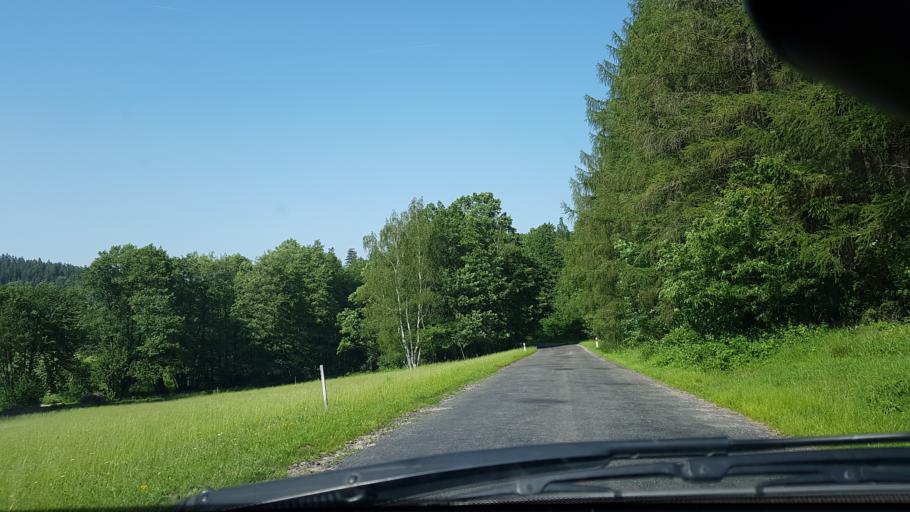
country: PL
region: Lower Silesian Voivodeship
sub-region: Powiat zabkowicki
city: Budzow
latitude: 50.5583
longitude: 16.6631
